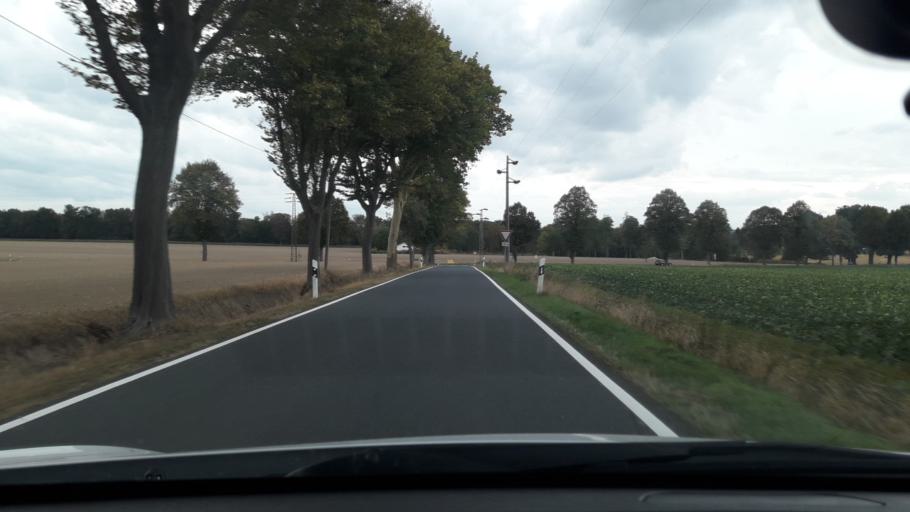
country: DE
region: Lower Saxony
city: Gielde
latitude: 52.0521
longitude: 10.4779
